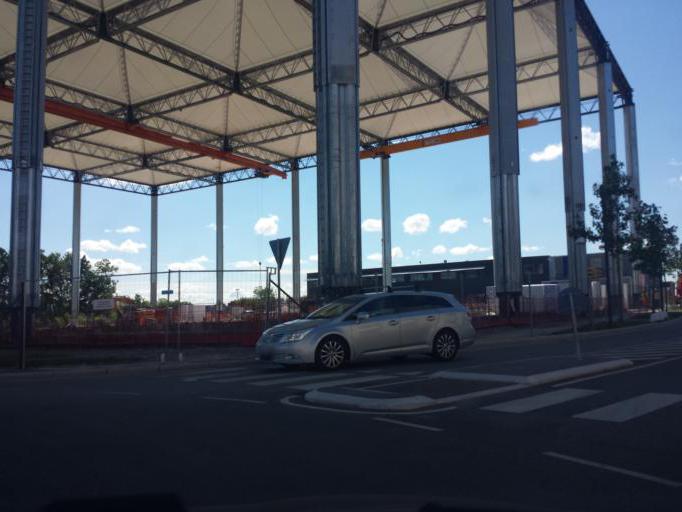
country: DK
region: Capital Region
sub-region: Egedal Kommune
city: Smorumnedre
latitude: 55.7542
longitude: 12.2998
